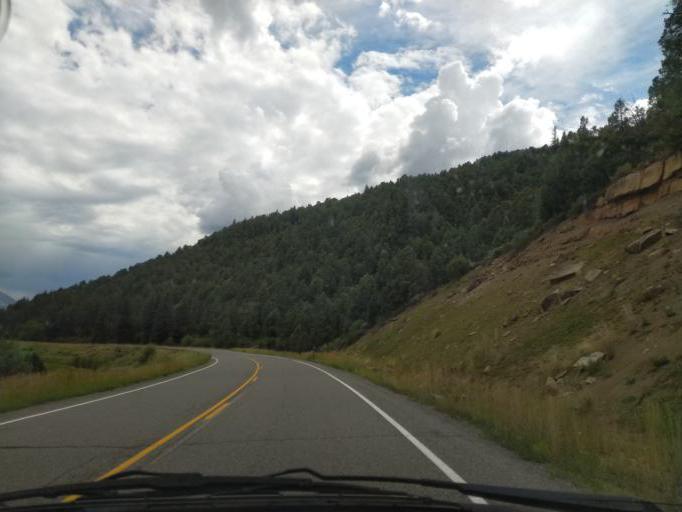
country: US
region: Colorado
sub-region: Delta County
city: Paonia
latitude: 39.0194
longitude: -107.3635
